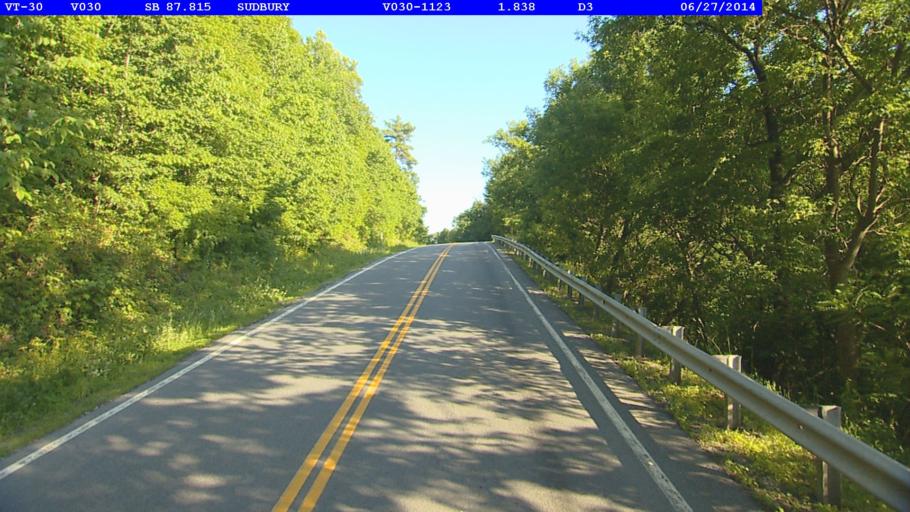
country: US
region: Vermont
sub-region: Rutland County
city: Brandon
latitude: 43.7746
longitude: -73.2026
